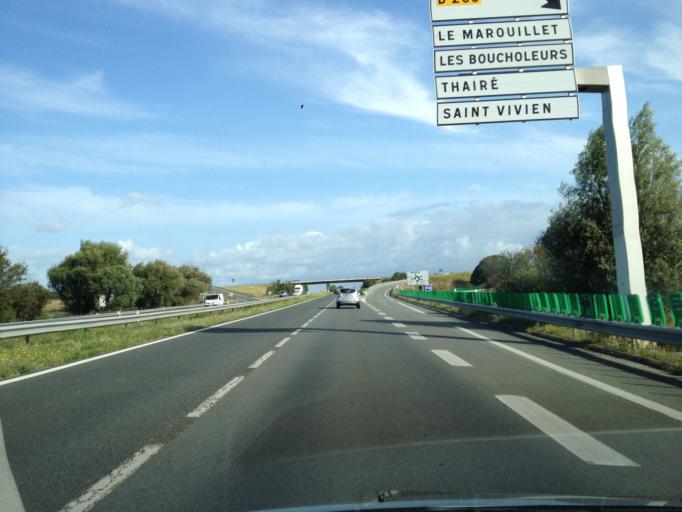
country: FR
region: Poitou-Charentes
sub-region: Departement de la Charente-Maritime
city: Chatelaillon-Plage
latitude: 46.0607
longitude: -1.0601
